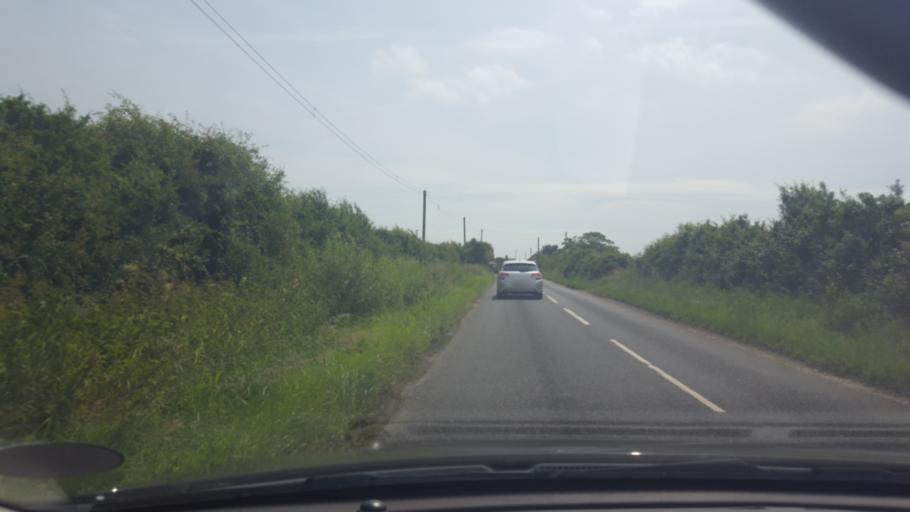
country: GB
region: England
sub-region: Essex
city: Clacton-on-Sea
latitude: 51.8183
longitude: 1.1860
